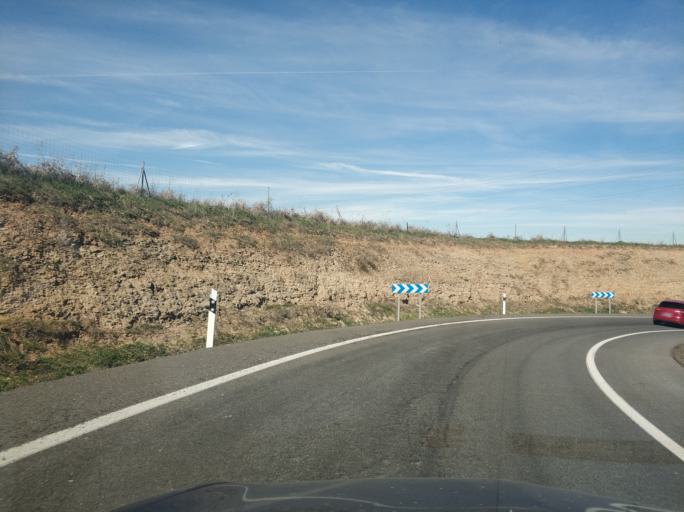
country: ES
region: Castille and Leon
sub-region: Provincia de Valladolid
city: Tordesillas
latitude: 41.5052
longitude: -4.9866
